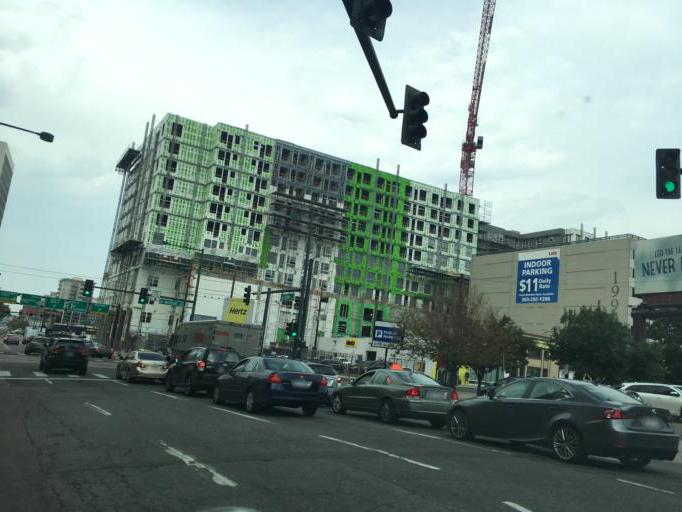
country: US
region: Colorado
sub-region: Denver County
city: Denver
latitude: 39.7479
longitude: -104.9862
